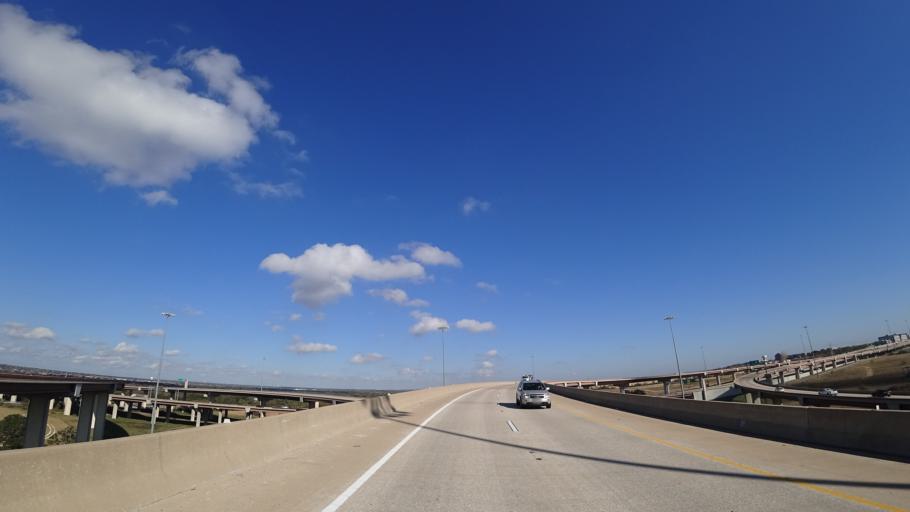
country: US
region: Texas
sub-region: Travis County
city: Wells Branch
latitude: 30.4746
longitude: -97.7029
